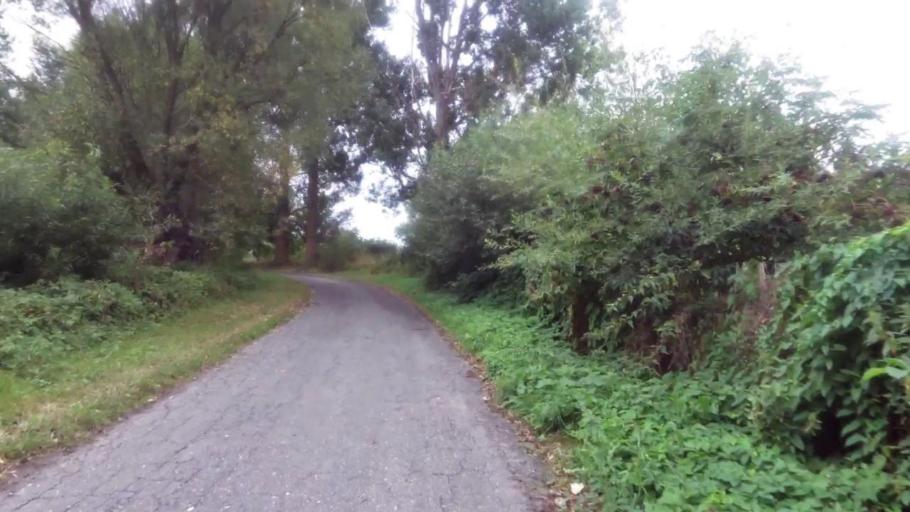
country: PL
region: West Pomeranian Voivodeship
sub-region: Powiat mysliborski
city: Boleszkowice
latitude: 52.6769
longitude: 14.6166
